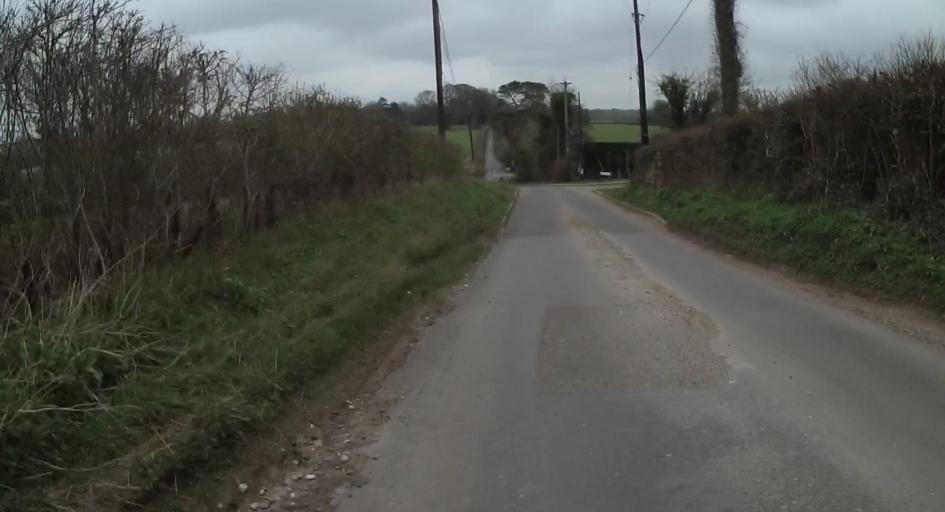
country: GB
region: England
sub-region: Hampshire
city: Four Marks
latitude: 51.0866
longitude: -1.0975
